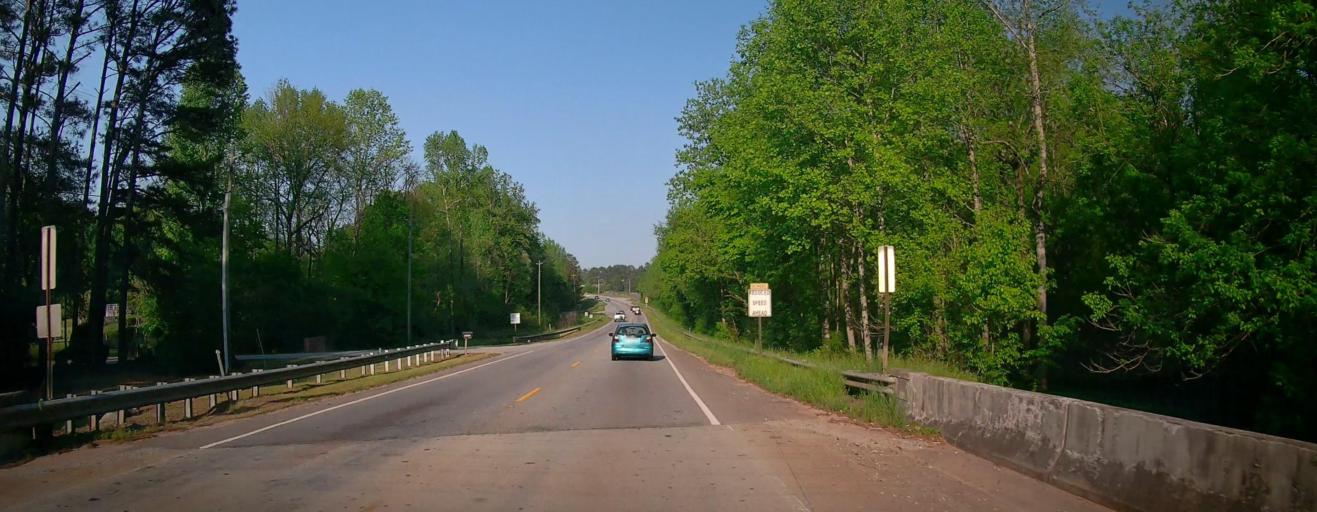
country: US
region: Georgia
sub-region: Newton County
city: Covington
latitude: 33.5667
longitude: -83.8612
